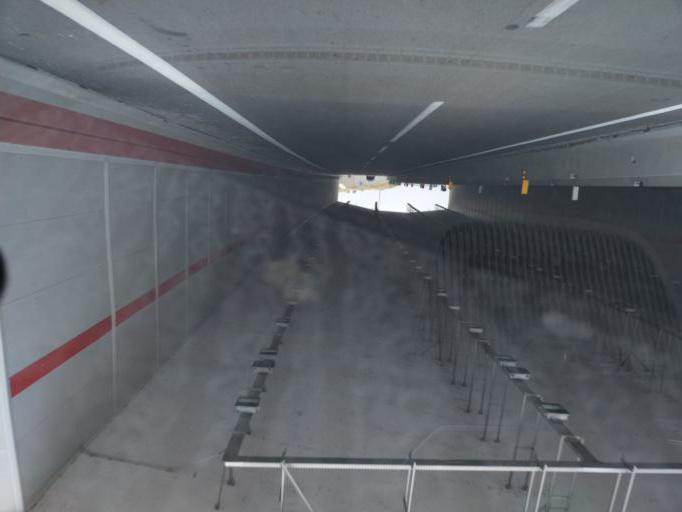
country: IT
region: Sicily
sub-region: Agrigento
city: Castrofilippo
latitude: 37.3779
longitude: 13.7923
